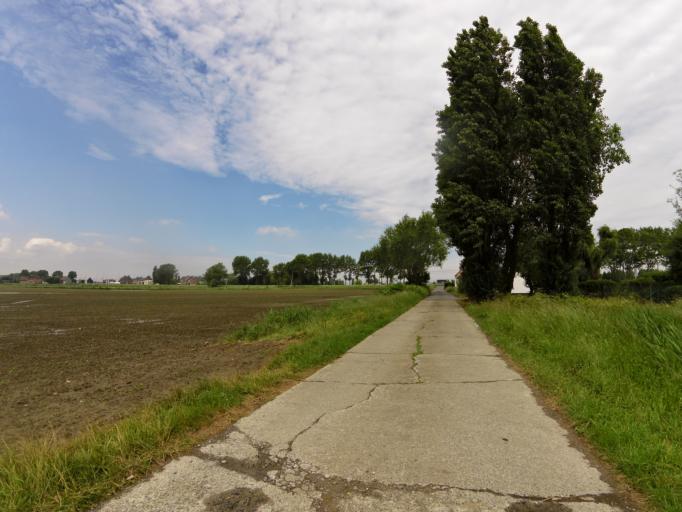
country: BE
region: Flanders
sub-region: Provincie West-Vlaanderen
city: Middelkerke
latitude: 51.1523
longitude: 2.8064
